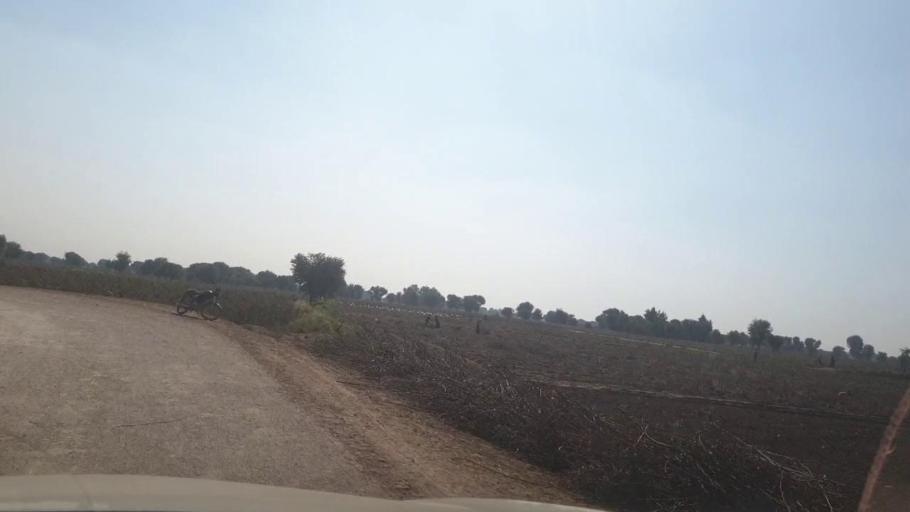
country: PK
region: Sindh
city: Bhan
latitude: 26.5796
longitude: 67.7009
